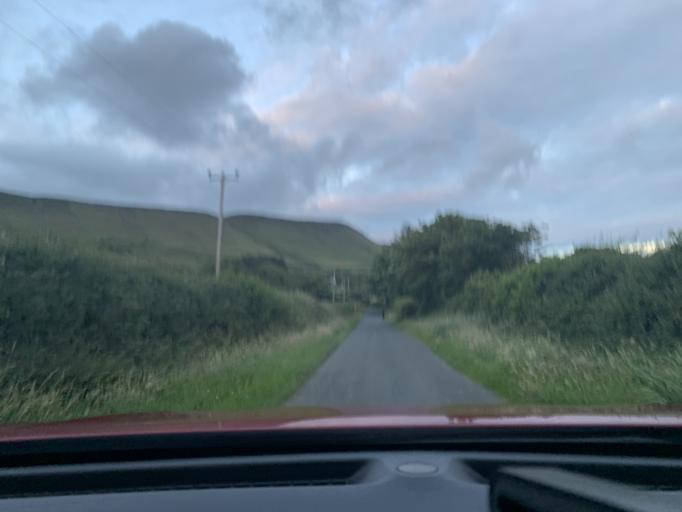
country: IE
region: Connaught
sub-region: Sligo
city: Sligo
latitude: 54.3536
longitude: -8.4901
